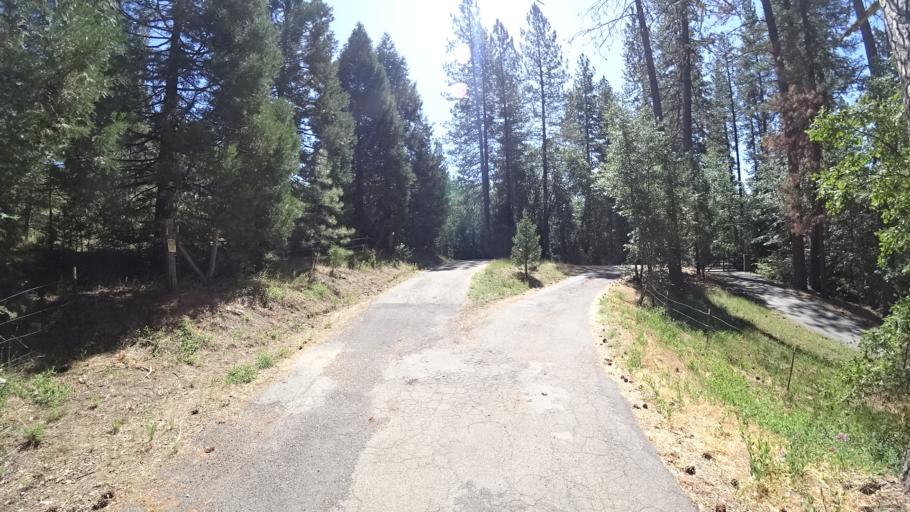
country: US
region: California
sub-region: Amador County
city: Pioneer
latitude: 38.3870
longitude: -120.4988
